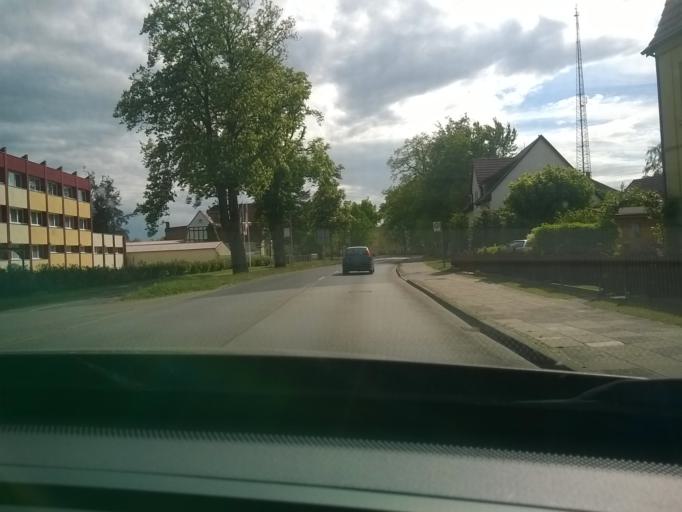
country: DE
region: Brandenburg
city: Wittstock
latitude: 53.1671
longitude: 12.4950
